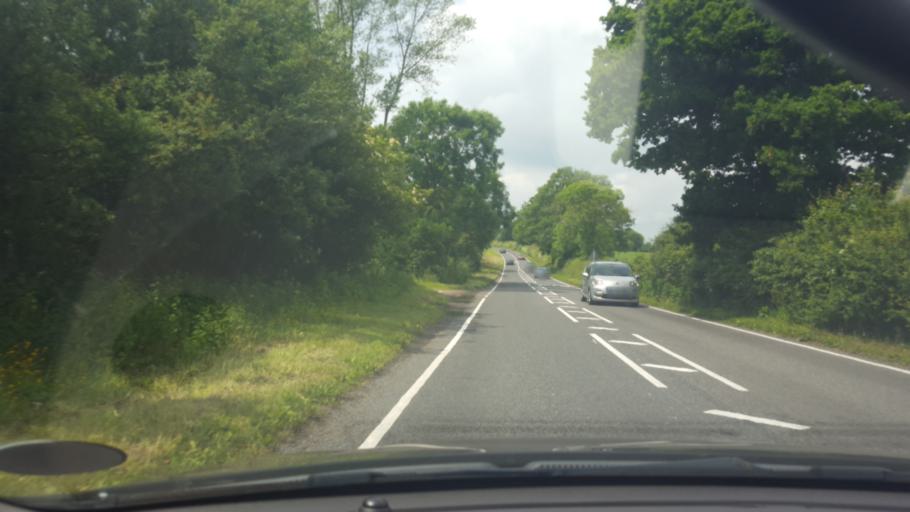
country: GB
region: England
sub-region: Essex
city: Little Clacton
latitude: 51.8602
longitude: 1.1310
